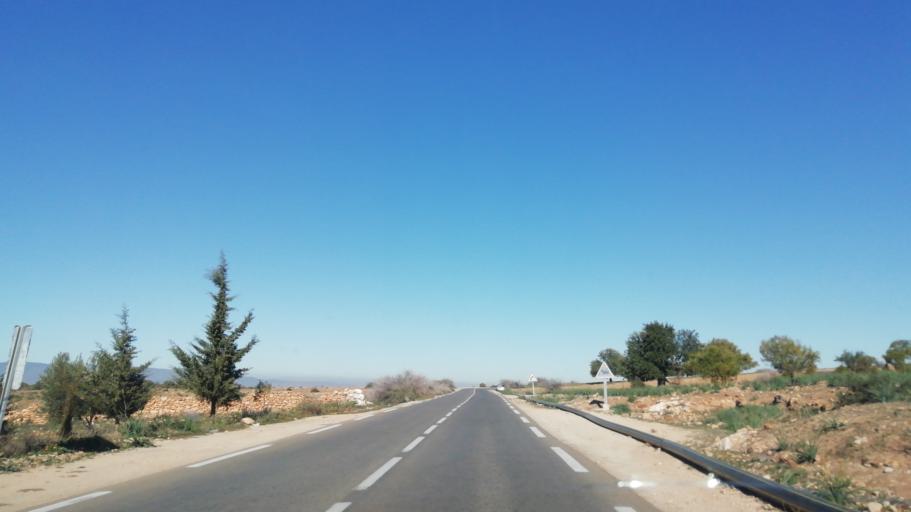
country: DZ
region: Tlemcen
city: Beni Mester
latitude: 34.8181
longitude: -1.6146
